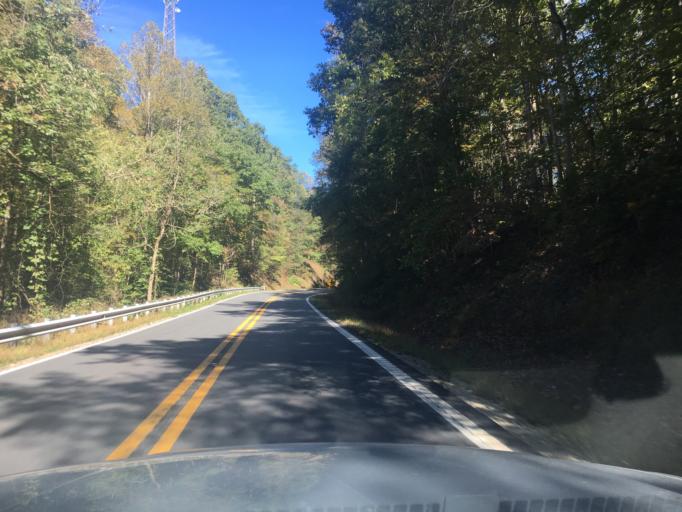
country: US
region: North Carolina
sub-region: Burke County
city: Glen Alpine
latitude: 35.5817
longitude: -81.8381
